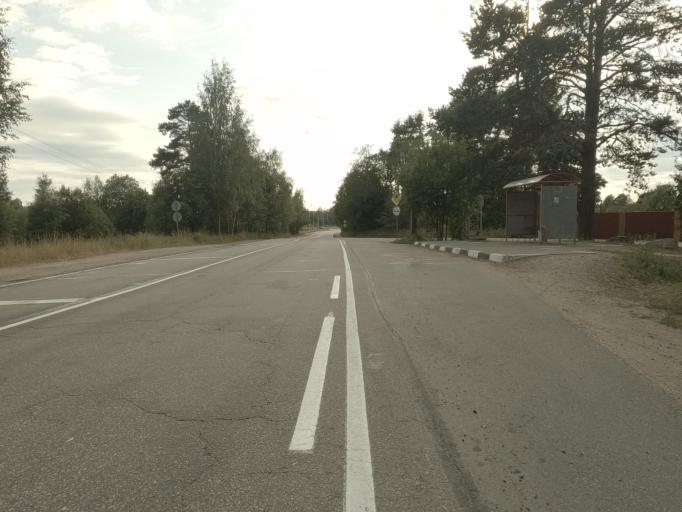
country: RU
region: Leningrad
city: Lesogorskiy
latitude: 60.8580
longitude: 28.9605
